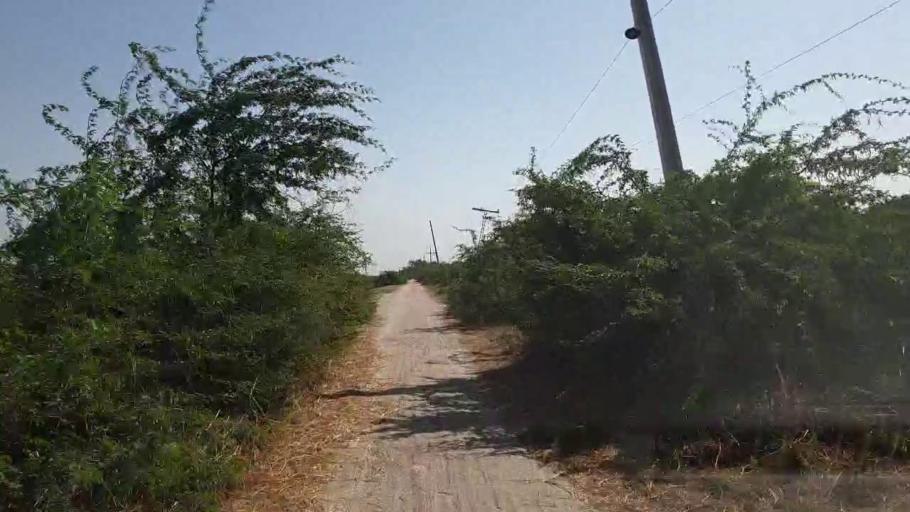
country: PK
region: Sindh
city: Tando Bago
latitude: 24.6445
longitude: 68.9872
